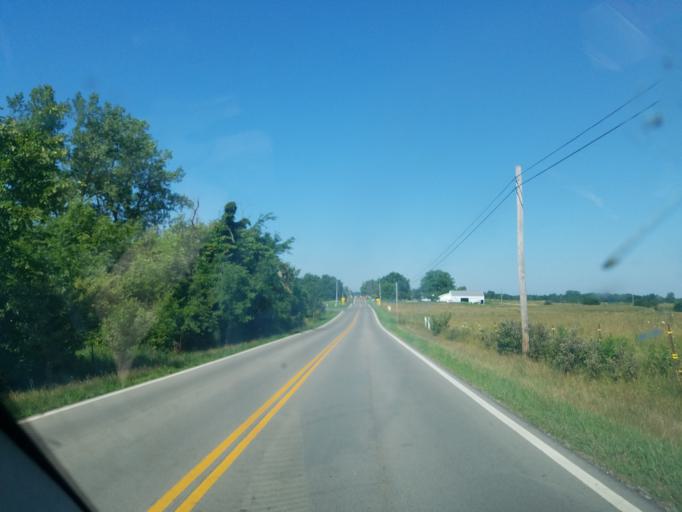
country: US
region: Ohio
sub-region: Logan County
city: Northwood
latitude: 40.4559
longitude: -83.7188
